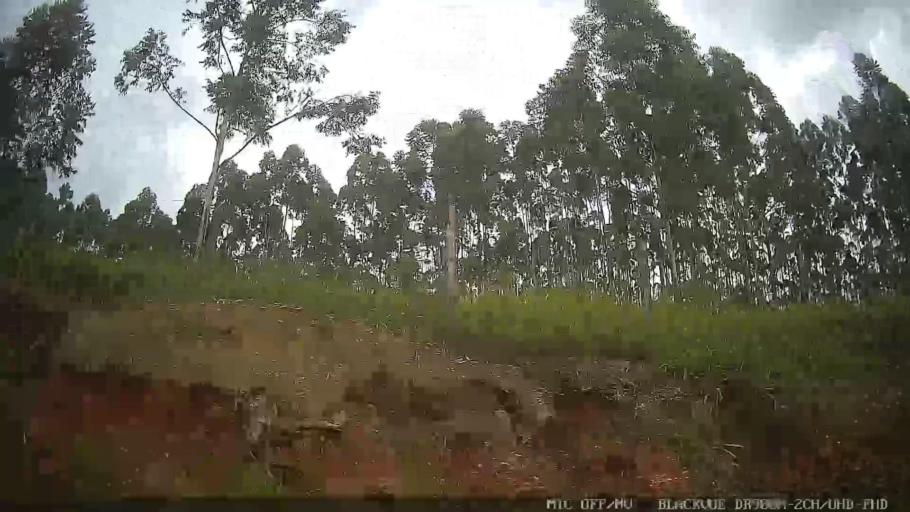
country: BR
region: Sao Paulo
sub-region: Mogi das Cruzes
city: Mogi das Cruzes
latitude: -23.4424
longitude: -46.2291
